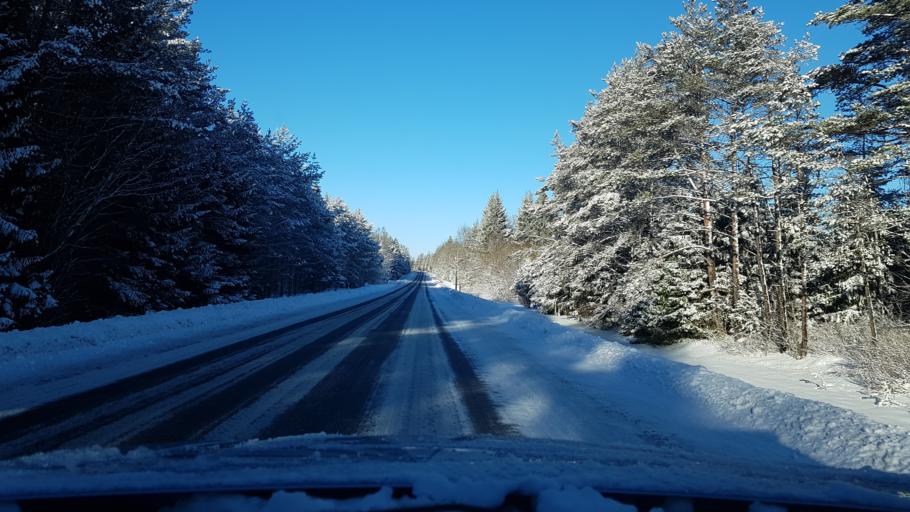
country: EE
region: Hiiumaa
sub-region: Kaerdla linn
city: Kardla
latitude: 58.9715
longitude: 22.8250
